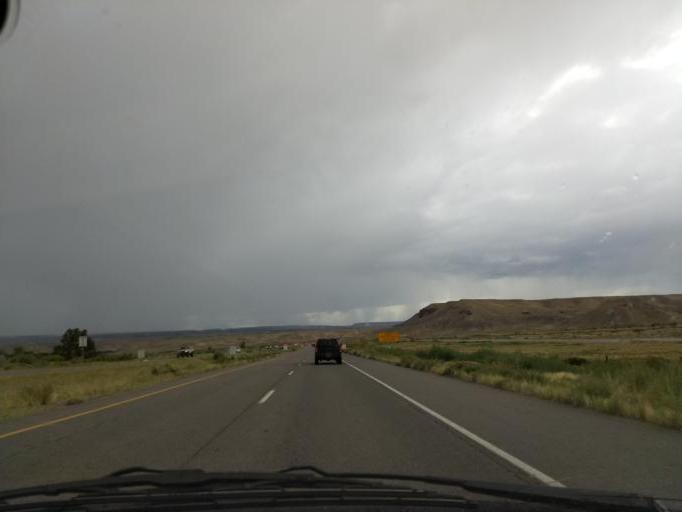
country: US
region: Colorado
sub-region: Delta County
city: Delta
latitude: 38.7568
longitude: -108.1477
